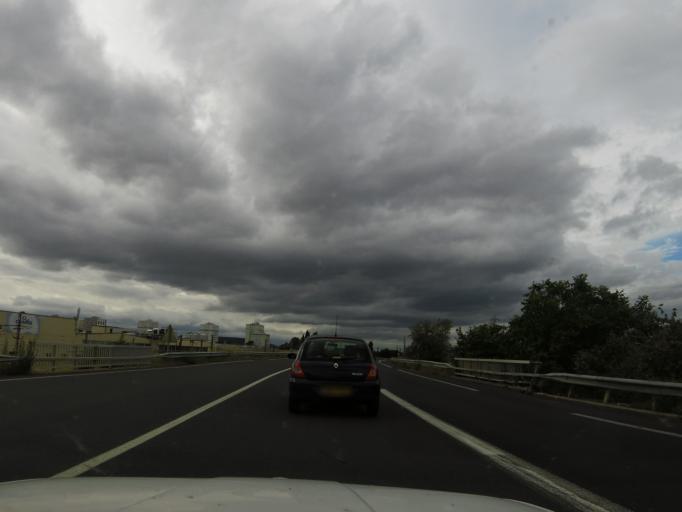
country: FR
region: Auvergne
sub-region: Departement du Puy-de-Dome
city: Gerzat
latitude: 45.8076
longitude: 3.1316
